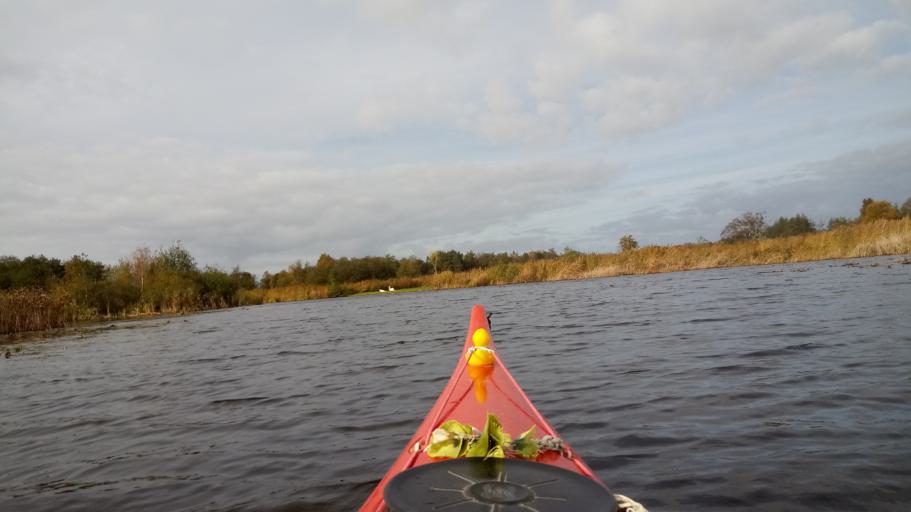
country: NL
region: Overijssel
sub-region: Gemeente Steenwijkerland
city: Sint Jansklooster
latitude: 52.6672
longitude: 6.0447
